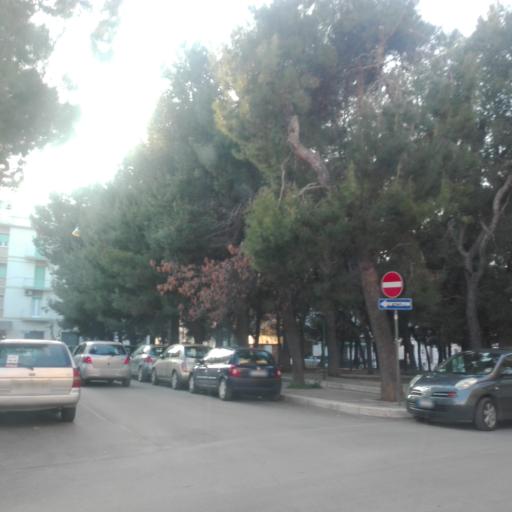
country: IT
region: Apulia
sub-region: Provincia di Bari
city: Corato
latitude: 41.1550
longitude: 16.4174
